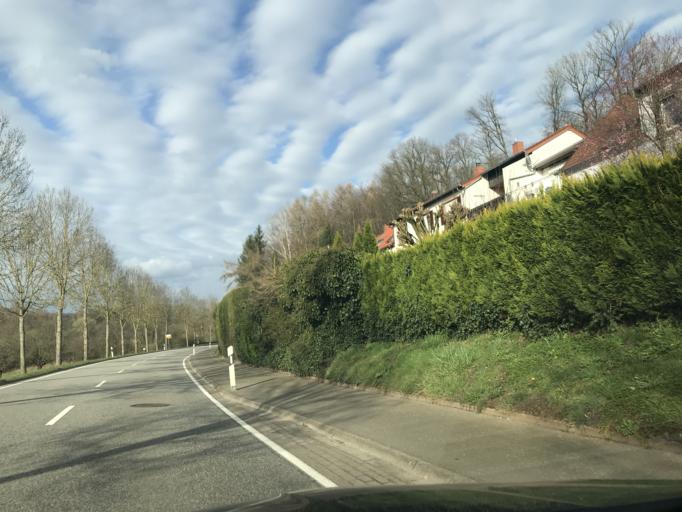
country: DE
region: Saarland
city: Blieskastel
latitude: 49.2042
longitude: 7.2465
